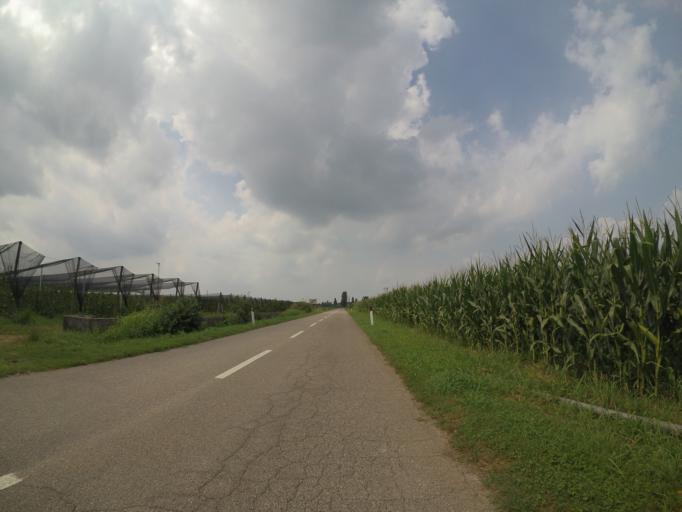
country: IT
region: Friuli Venezia Giulia
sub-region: Provincia di Udine
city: Sedegliano
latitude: 45.9969
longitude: 13.0157
